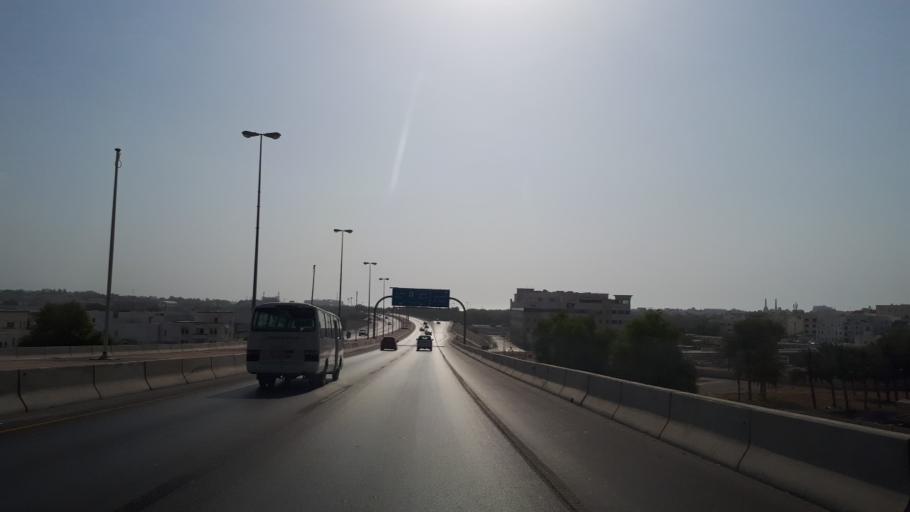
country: OM
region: Muhafazat Masqat
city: Muscat
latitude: 23.6161
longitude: 58.5007
